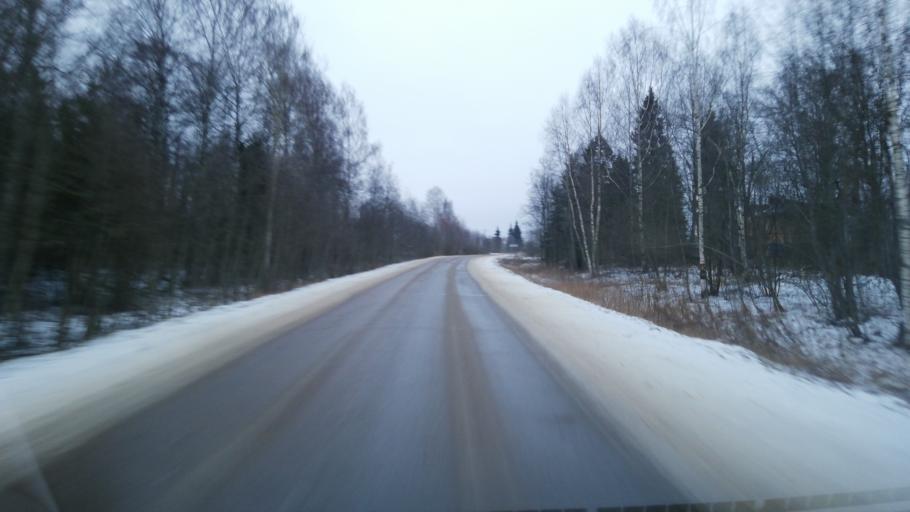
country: RU
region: Kostroma
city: Oktyabr'skiy
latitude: 57.7171
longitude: 41.1356
